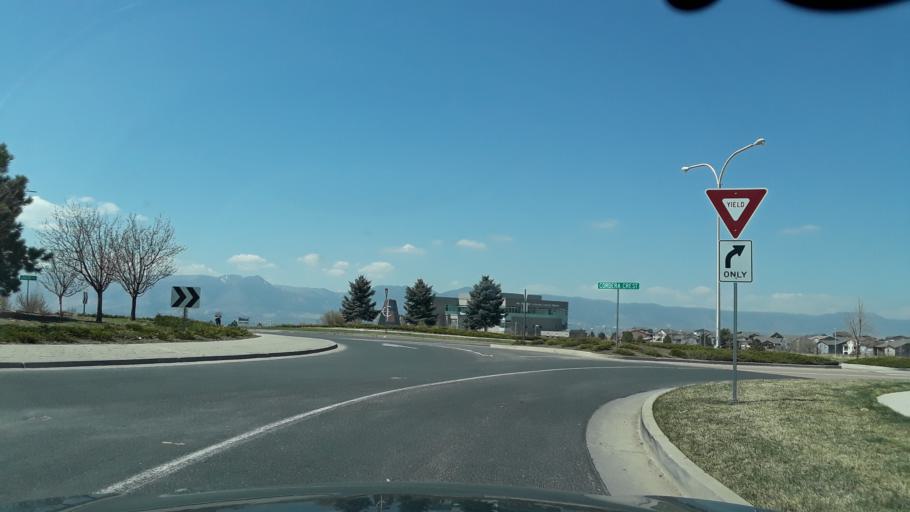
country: US
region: Colorado
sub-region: El Paso County
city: Black Forest
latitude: 38.9760
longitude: -104.7439
